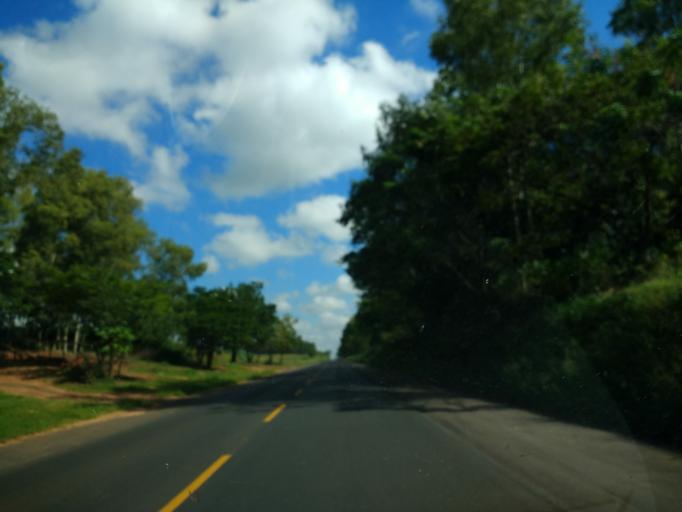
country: BR
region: Parana
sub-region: Umuarama
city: Umuarama
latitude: -23.8574
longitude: -53.3786
